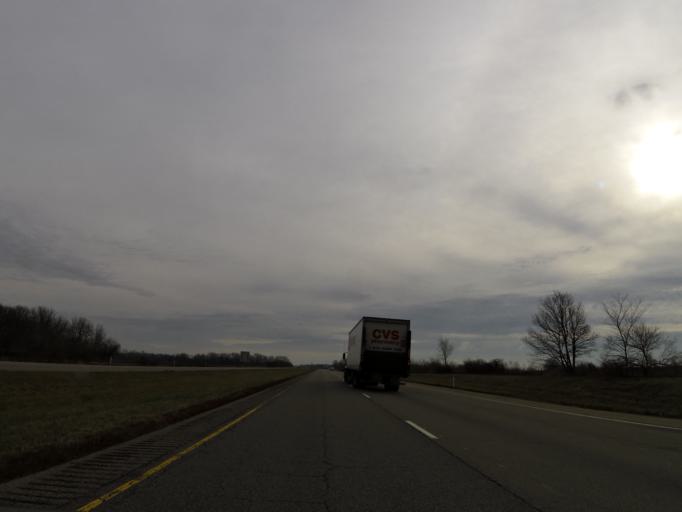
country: US
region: Indiana
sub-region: Fountain County
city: Veedersburg
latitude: 40.1031
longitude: -87.0638
